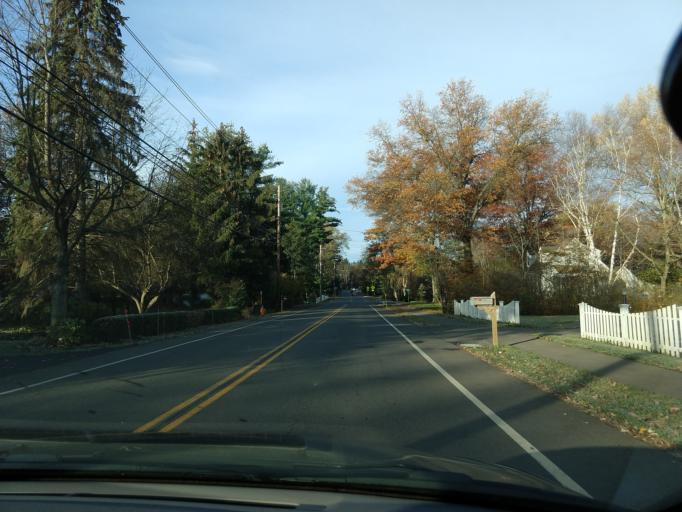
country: US
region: New York
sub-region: Tompkins County
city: Northeast Ithaca
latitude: 42.4671
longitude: -76.4671
